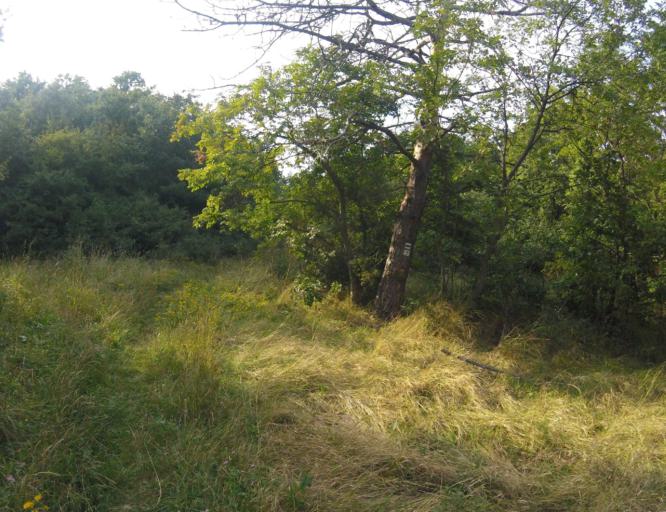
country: HU
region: Pest
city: Nagykovacsi
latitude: 47.6767
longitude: 19.0181
